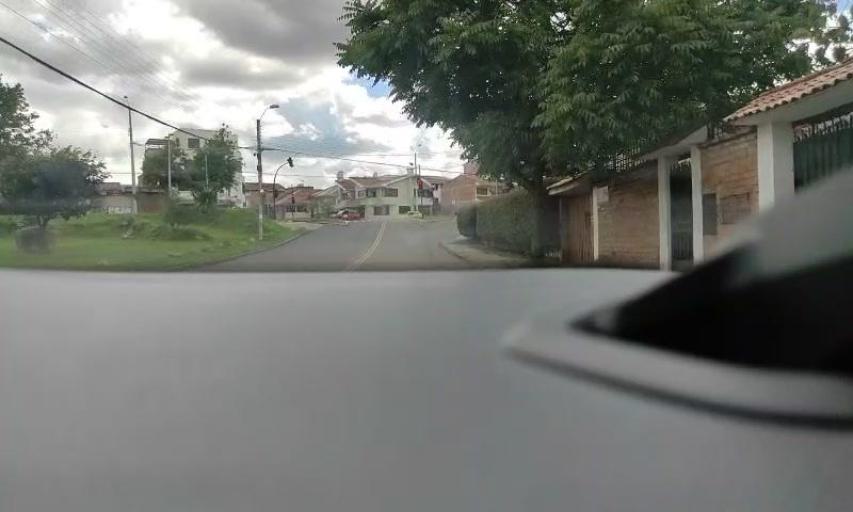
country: EC
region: Azuay
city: Cuenca
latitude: -2.9087
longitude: -79.0317
